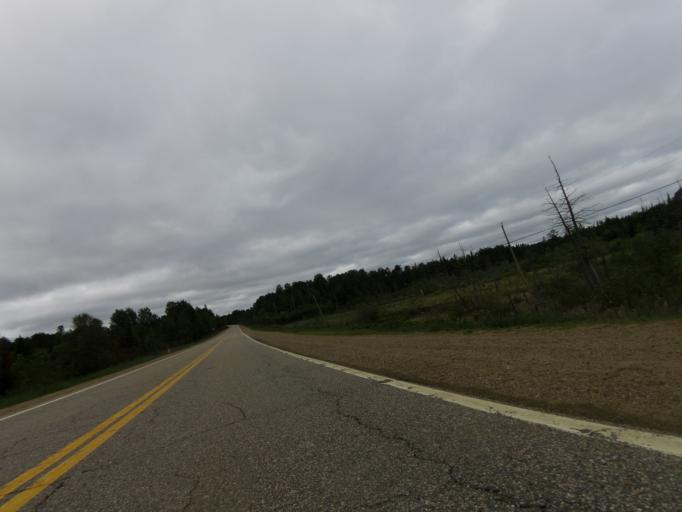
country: CA
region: Quebec
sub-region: Outaouais
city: Shawville
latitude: 45.8770
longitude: -76.4002
